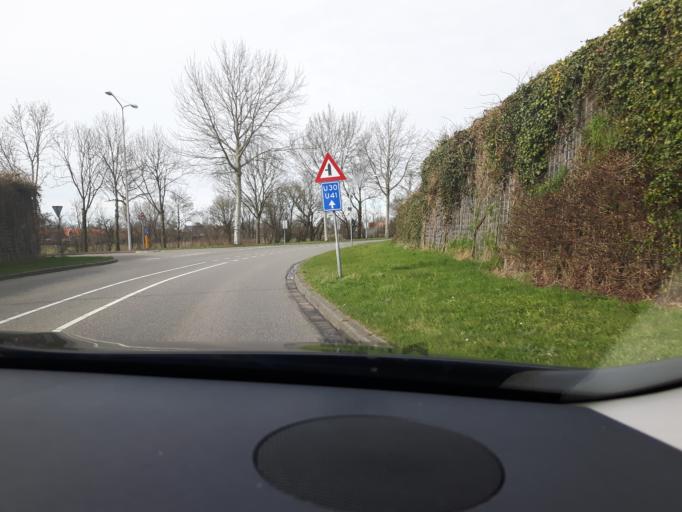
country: NL
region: Zeeland
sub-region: Gemeente Middelburg
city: Middelburg
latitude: 51.5108
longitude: 3.6082
